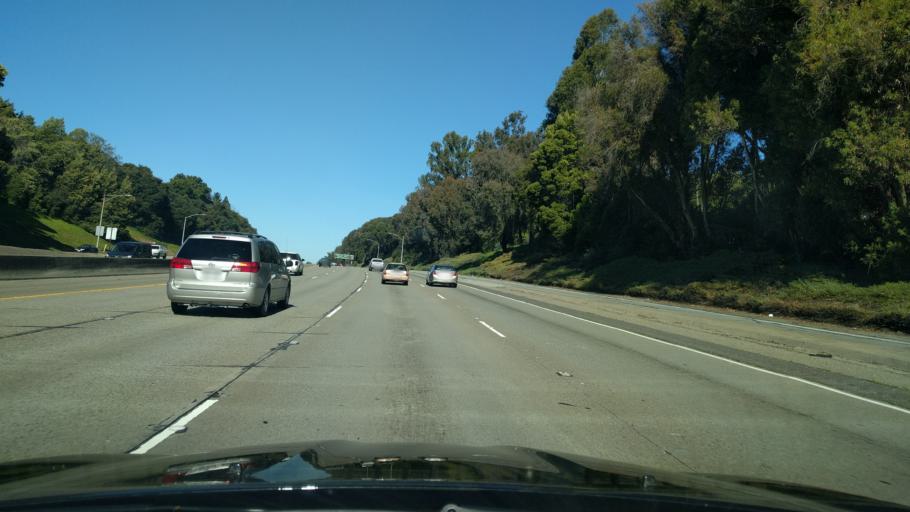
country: US
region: California
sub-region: Alameda County
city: San Leandro
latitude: 37.7730
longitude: -122.1576
